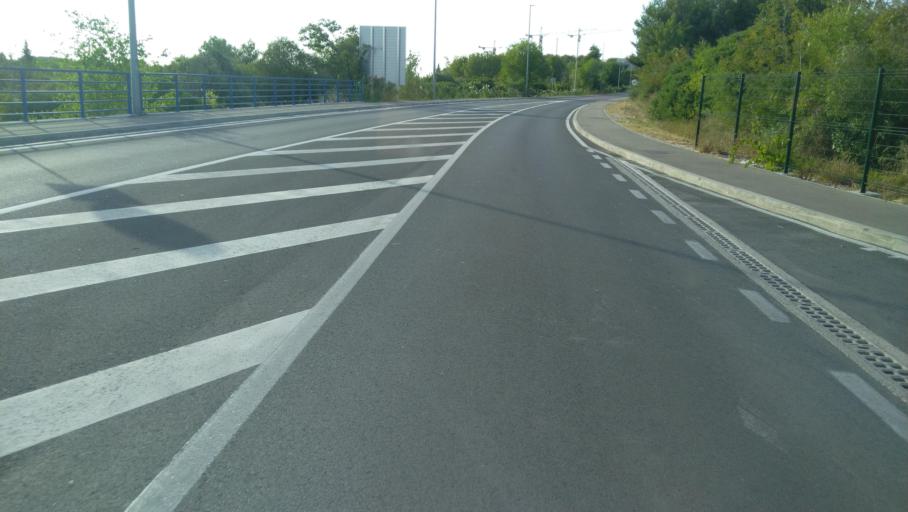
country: HR
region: Sibensko-Kniniska
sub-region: Grad Sibenik
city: Sibenik
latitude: 43.7168
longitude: 15.9117
